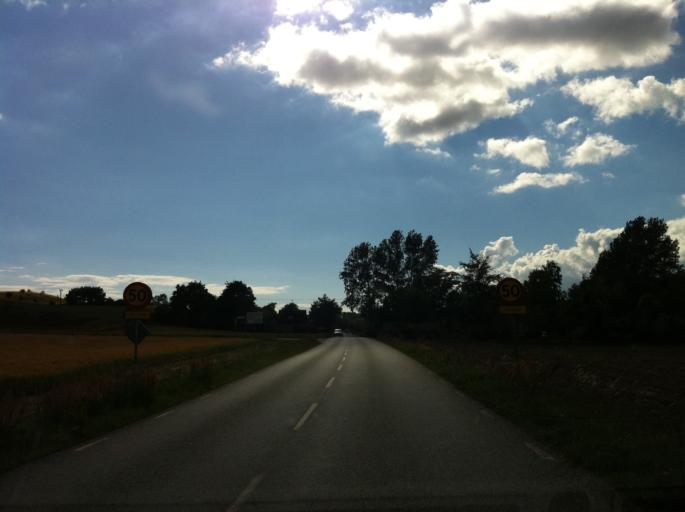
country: SE
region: Skane
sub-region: Ystads Kommun
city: Kopingebro
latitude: 55.3957
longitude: 14.0370
